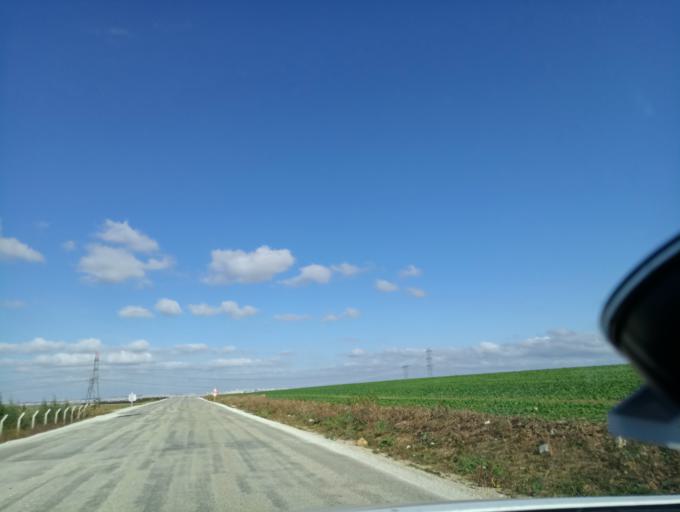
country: TR
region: Tekirdag
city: Corlu
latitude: 41.0554
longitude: 27.8349
